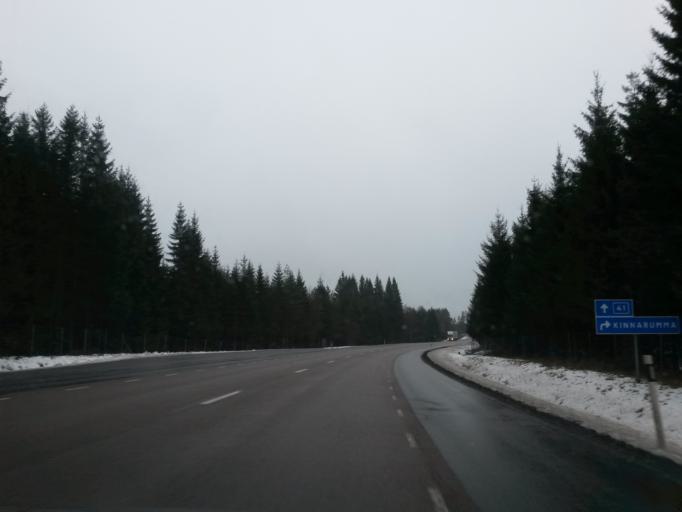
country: SE
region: Vaestra Goetaland
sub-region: Boras Kommun
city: Viskafors
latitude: 57.6166
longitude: 12.8806
